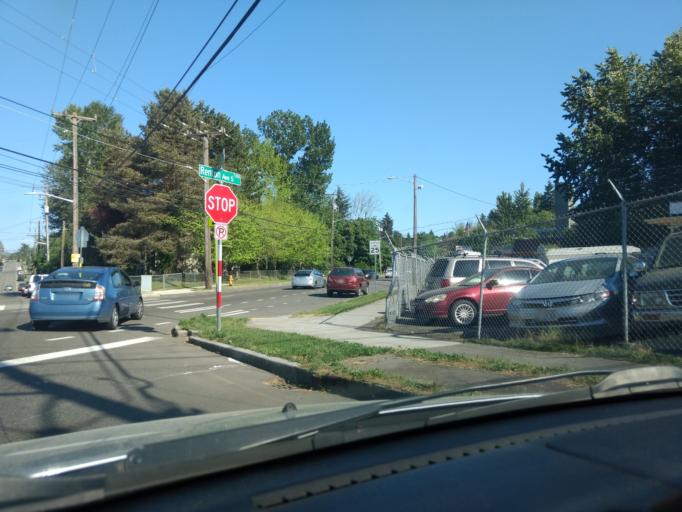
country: US
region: Washington
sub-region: King County
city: Bryn Mawr-Skyway
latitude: 47.5169
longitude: -122.2699
